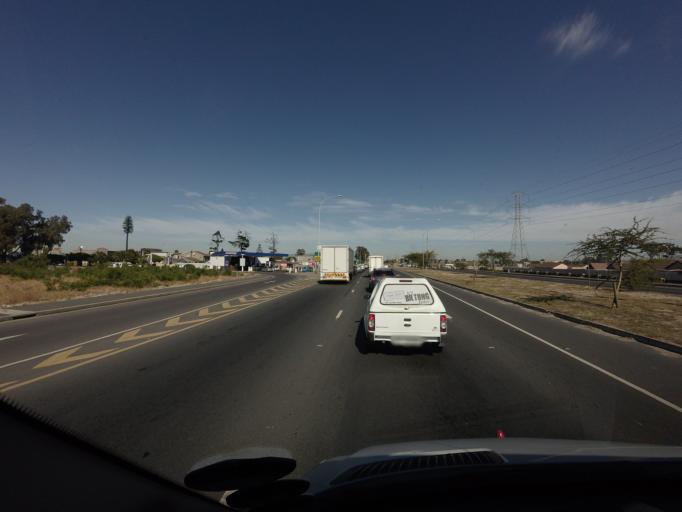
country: ZA
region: Western Cape
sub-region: City of Cape Town
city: Kraaifontein
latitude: -33.9560
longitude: 18.6731
